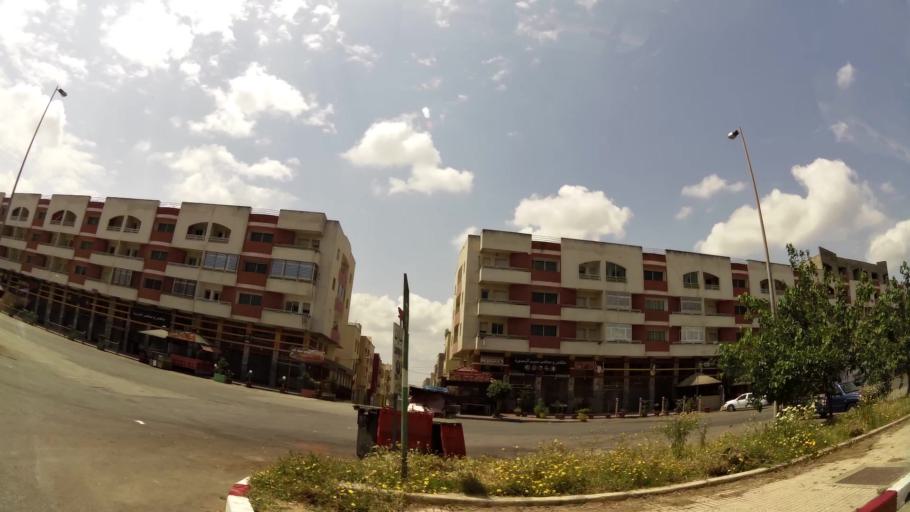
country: MA
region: Gharb-Chrarda-Beni Hssen
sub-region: Kenitra Province
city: Kenitra
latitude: 34.0122
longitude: -6.5380
